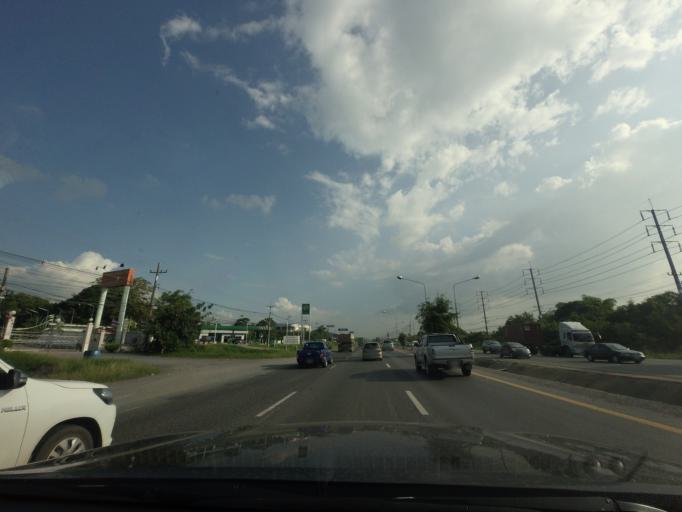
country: TH
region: Sara Buri
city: Chaloem Phra Kiat
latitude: 14.5825
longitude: 100.9002
